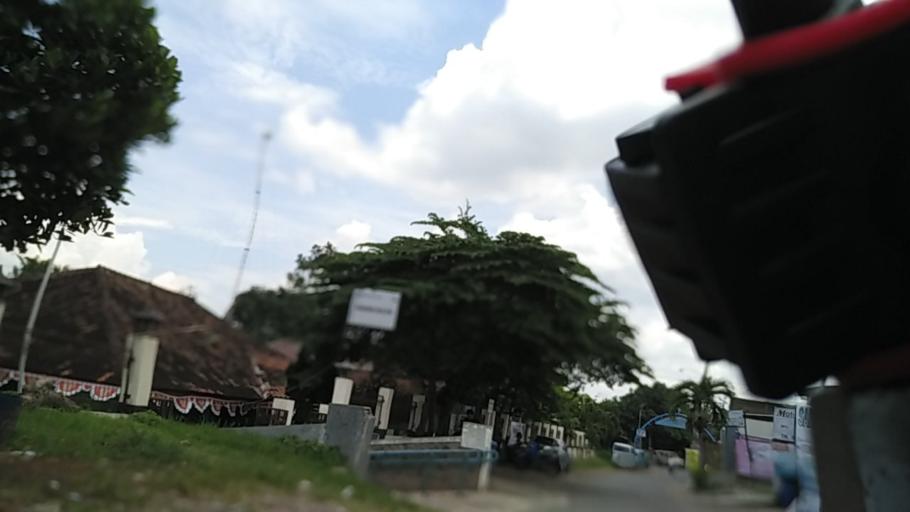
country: ID
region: Central Java
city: Semarang
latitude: -6.9982
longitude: 110.3471
